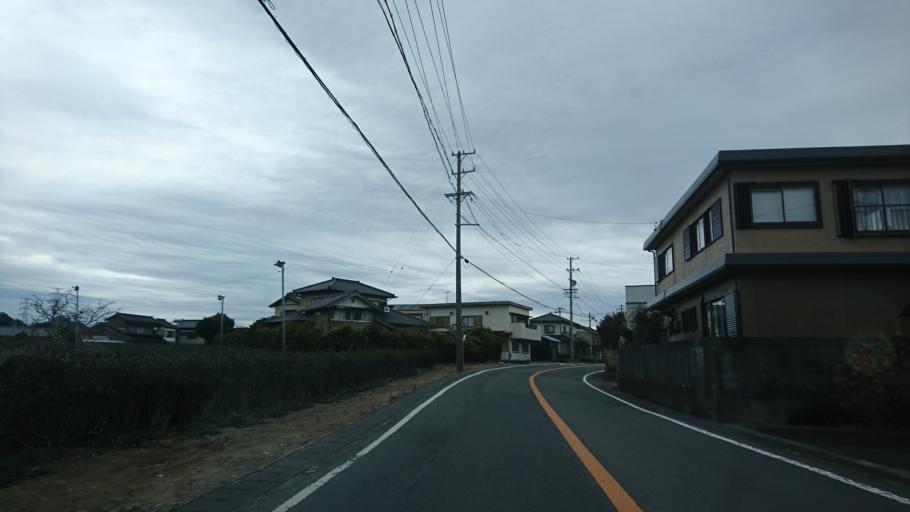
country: JP
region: Shizuoka
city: Kanaya
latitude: 34.7796
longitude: 138.1254
